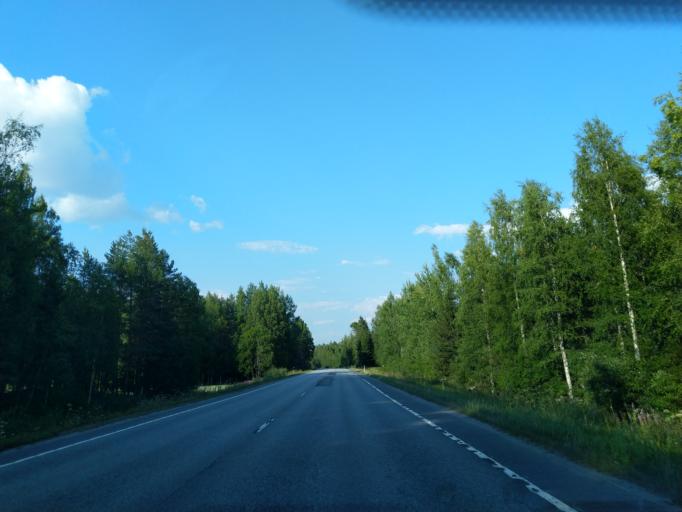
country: FI
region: Satakunta
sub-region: Pori
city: Laengelmaeki
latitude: 61.7522
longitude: 22.1197
